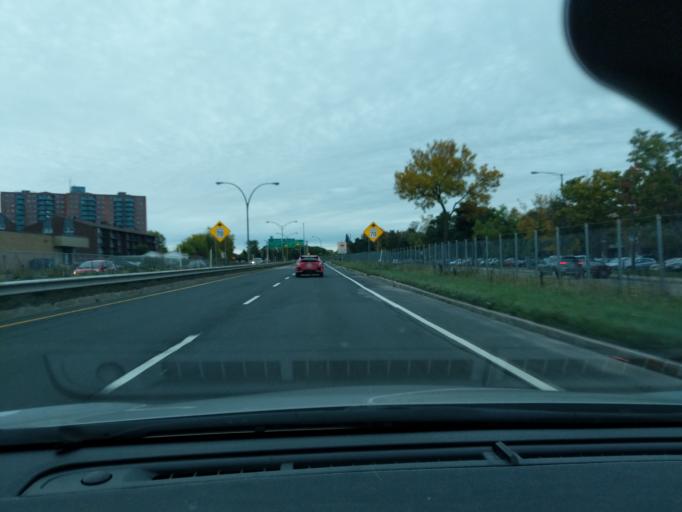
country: CA
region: Quebec
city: L'Ancienne-Lorette
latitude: 46.7636
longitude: -71.3109
